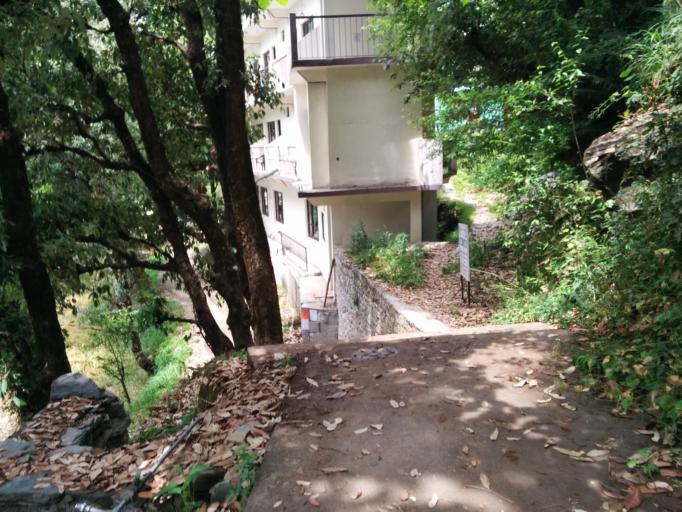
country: IN
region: Himachal Pradesh
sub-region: Kangra
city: Dharmsala
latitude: 32.2462
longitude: 76.3331
